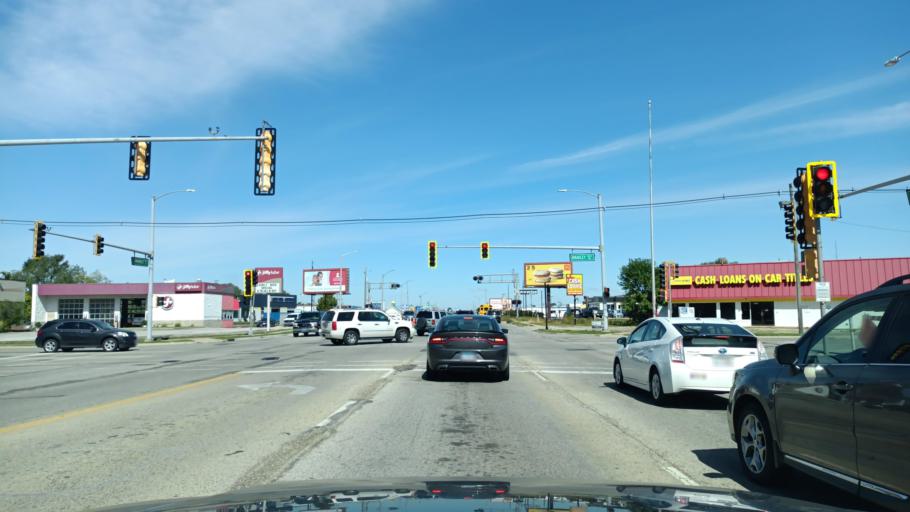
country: US
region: Illinois
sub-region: Champaign County
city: Champaign
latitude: 40.1266
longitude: -88.2580
